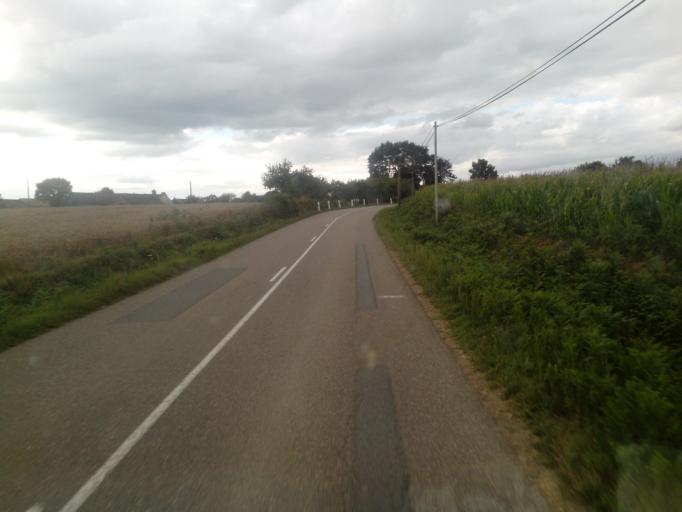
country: FR
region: Brittany
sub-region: Departement d'Ille-et-Vilaine
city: Maxent
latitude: 47.9737
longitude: -2.0218
